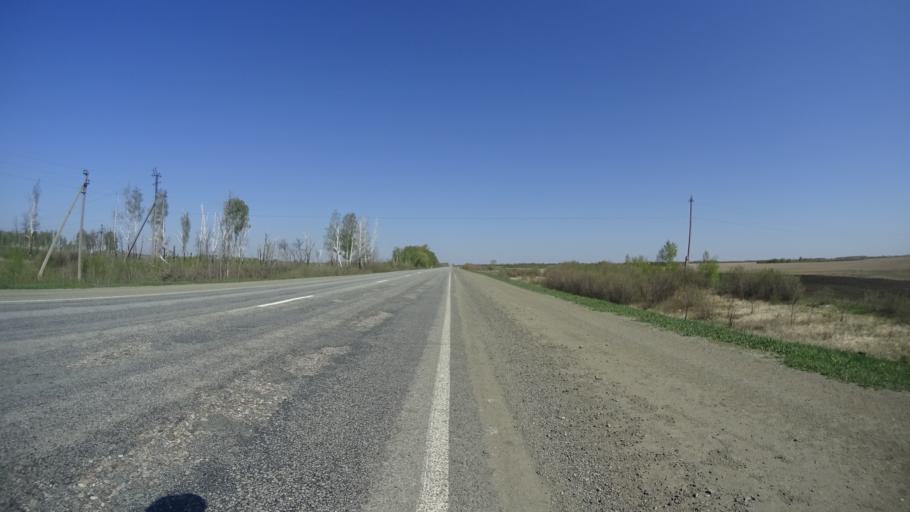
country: RU
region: Chelyabinsk
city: Troitsk
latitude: 54.1948
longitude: 61.4329
